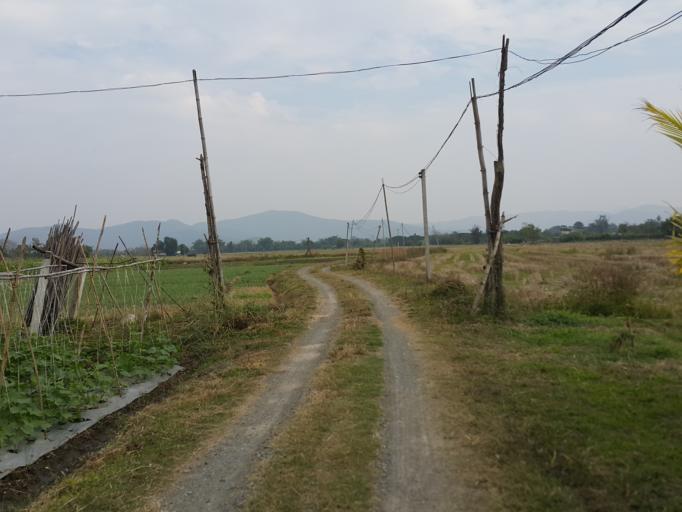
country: TH
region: Chiang Mai
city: San Kamphaeng
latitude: 18.8250
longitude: 99.1469
